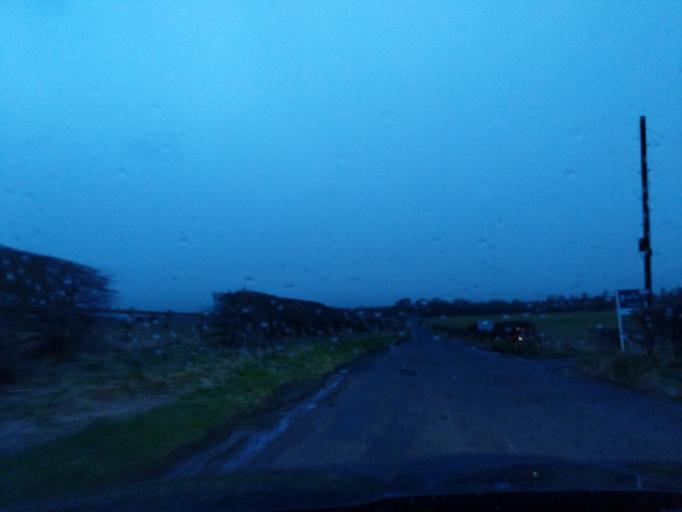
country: GB
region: England
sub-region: Northumberland
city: Ford
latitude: 55.7146
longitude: -2.1289
